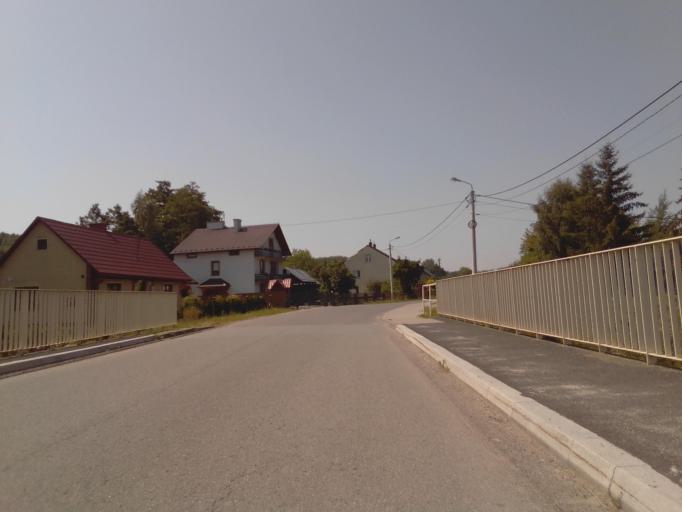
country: PL
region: Subcarpathian Voivodeship
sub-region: Powiat ropczycko-sedziszowski
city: Zagorzyce
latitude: 50.0506
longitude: 21.6660
